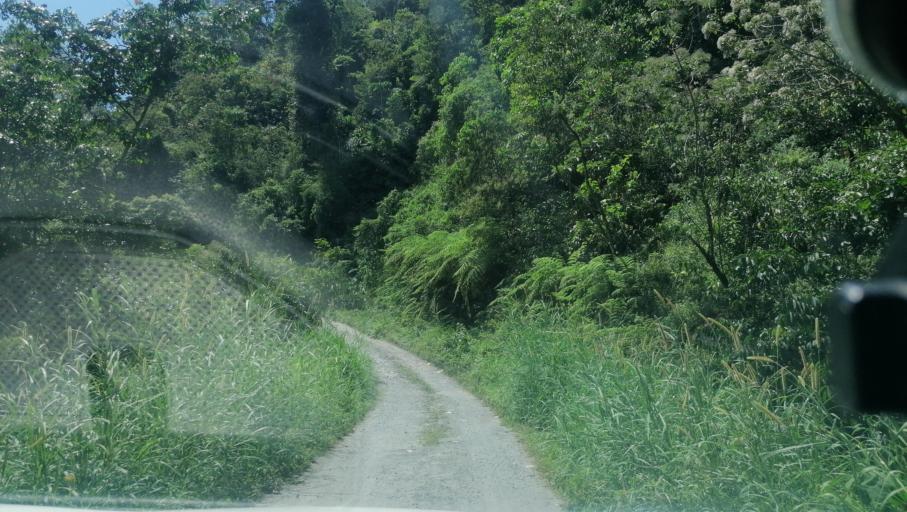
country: MX
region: Chiapas
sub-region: Union Juarez
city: Santo Domingo
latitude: 15.0684
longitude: -92.1378
